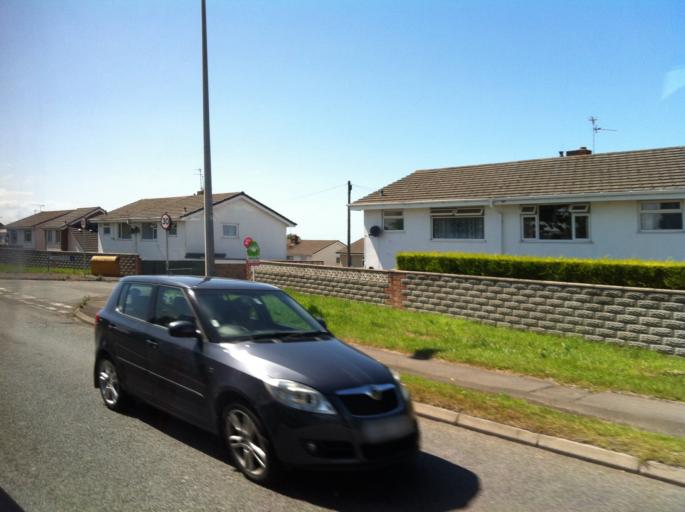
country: GB
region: Wales
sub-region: Vale of Glamorgan
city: Barry
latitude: 51.4237
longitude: -3.2749
